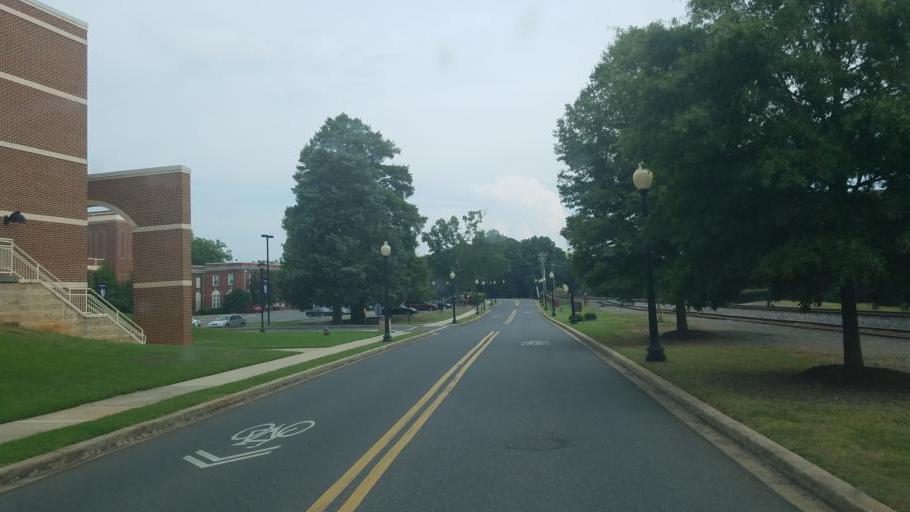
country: US
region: South Carolina
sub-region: York County
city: Rock Hill
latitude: 34.9374
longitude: -81.0327
